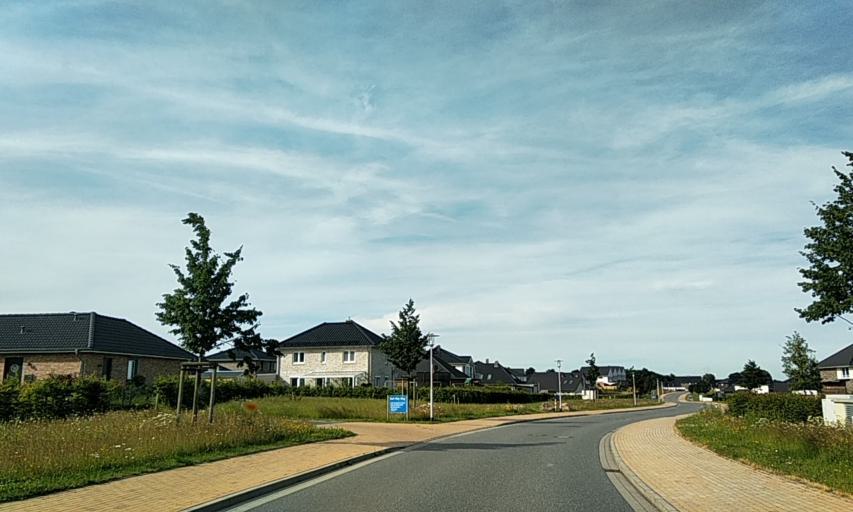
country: DE
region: Schleswig-Holstein
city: Schleswig
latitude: 54.5346
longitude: 9.5620
